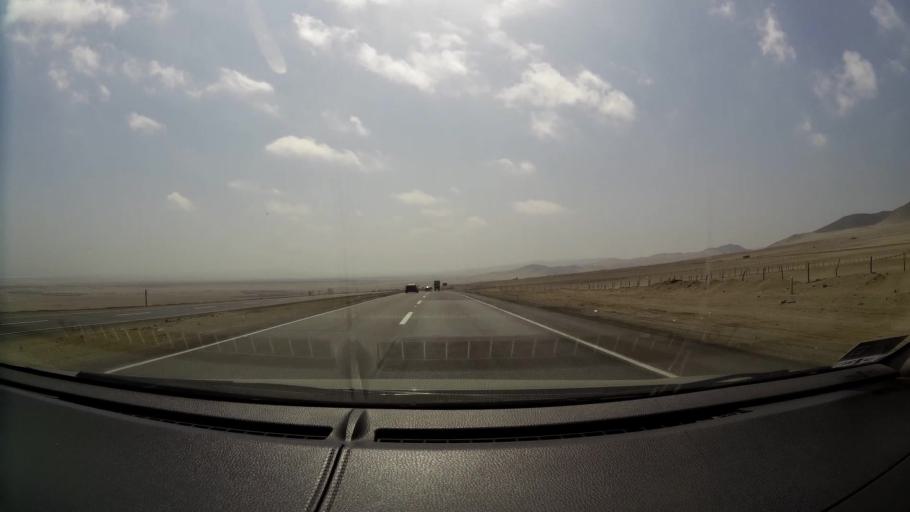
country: PE
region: Lima
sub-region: Huaura
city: Huacho
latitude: -11.3413
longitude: -77.4630
